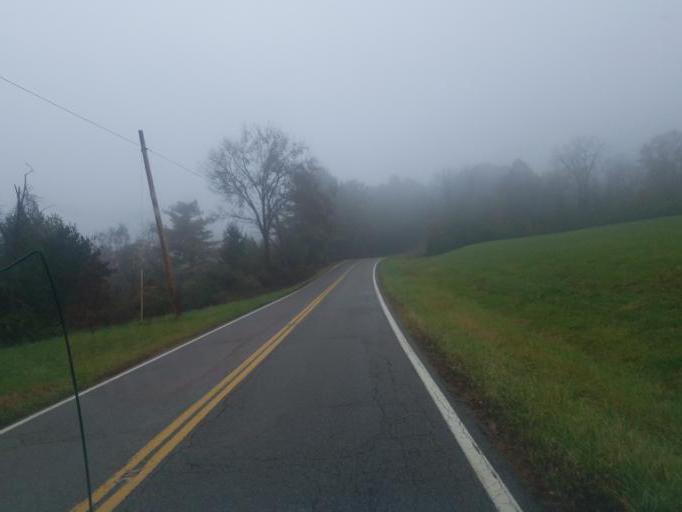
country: US
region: Ohio
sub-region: Morgan County
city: McConnelsville
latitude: 39.5359
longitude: -81.8009
